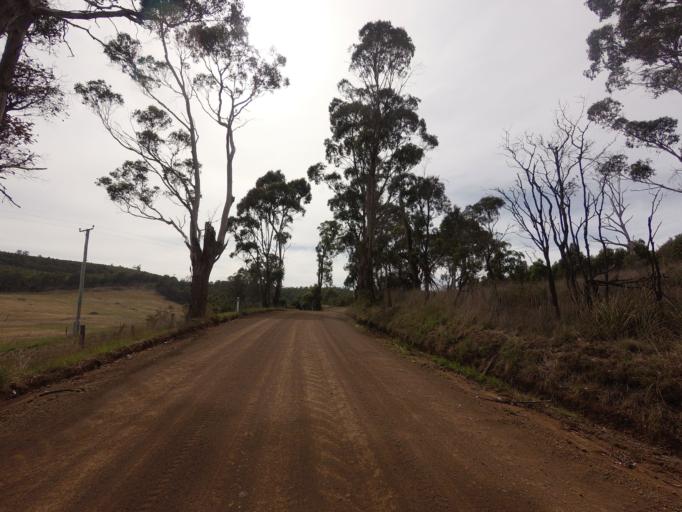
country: AU
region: Tasmania
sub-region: Sorell
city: Sorell
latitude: -42.4773
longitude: 147.5972
